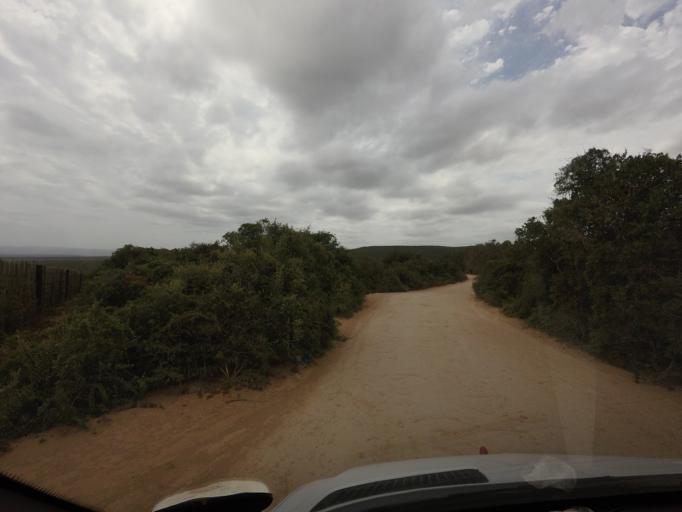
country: ZA
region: Eastern Cape
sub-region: Cacadu District Municipality
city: Kirkwood
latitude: -33.5176
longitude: 25.7613
